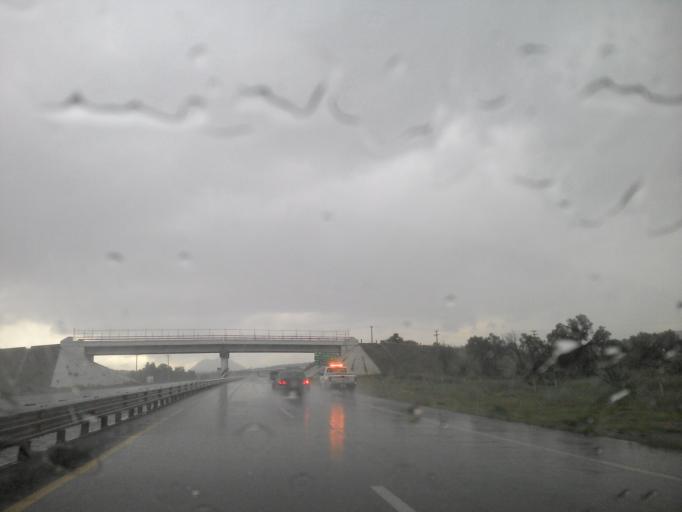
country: MX
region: Hidalgo
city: Zempoala
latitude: 19.8737
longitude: -98.6683
